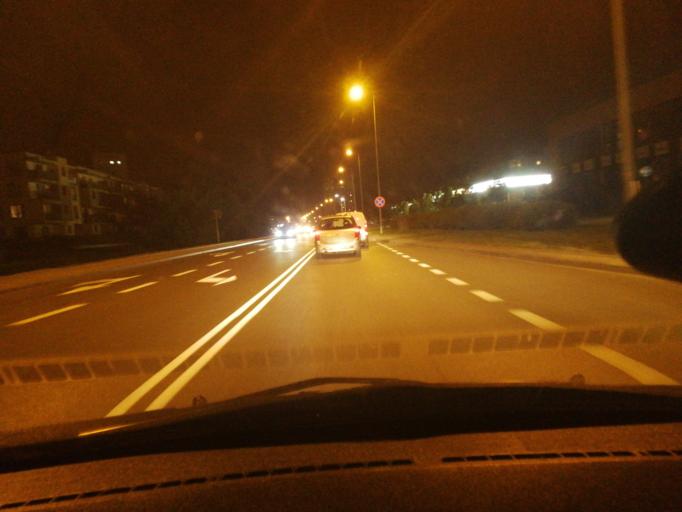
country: PL
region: Masovian Voivodeship
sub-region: Warszawa
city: Targowek
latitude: 52.2963
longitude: 21.0547
